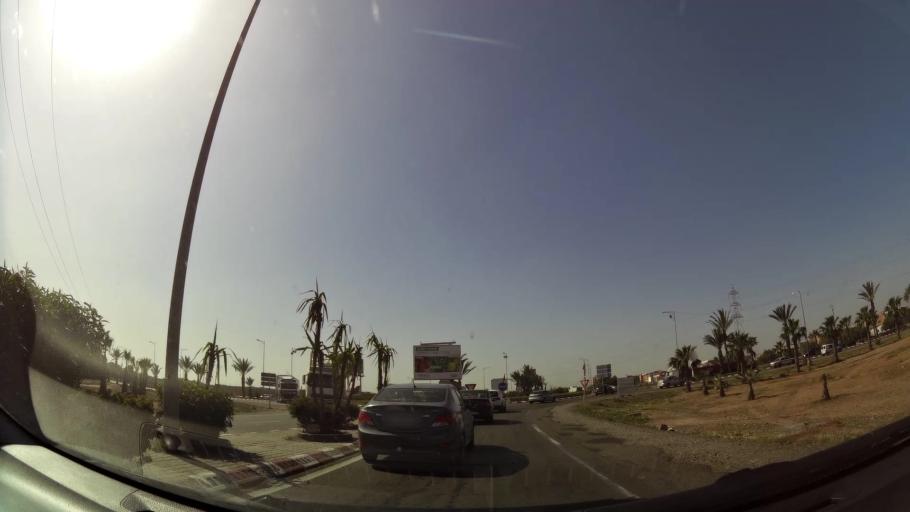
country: MA
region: Souss-Massa-Draa
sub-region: Inezgane-Ait Mellou
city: Inezgane
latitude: 30.3404
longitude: -9.4785
